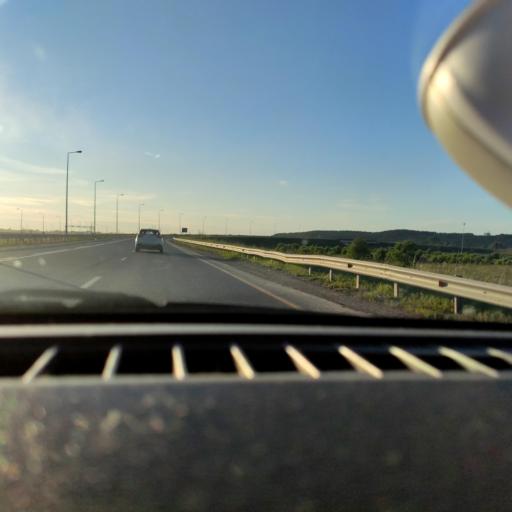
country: RU
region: Perm
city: Kondratovo
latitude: 57.9249
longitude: 56.1751
